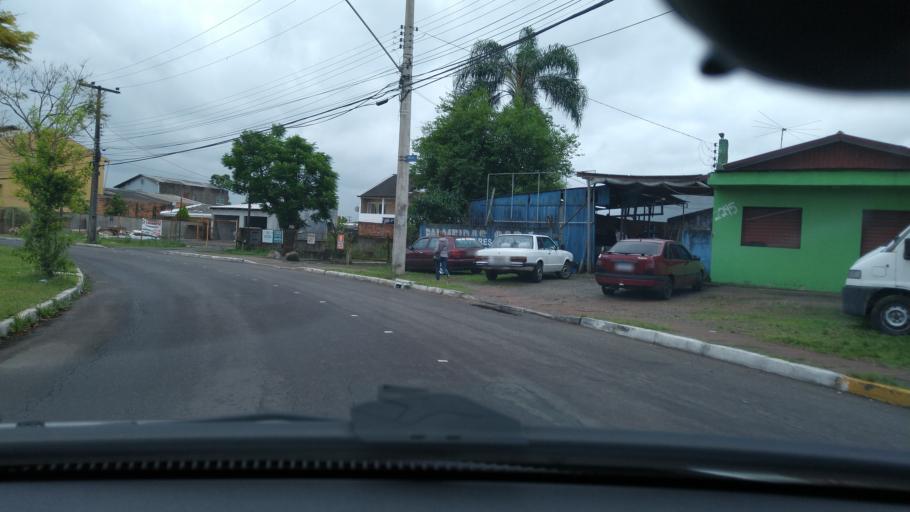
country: BR
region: Rio Grande do Sul
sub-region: Canoas
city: Canoas
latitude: -29.9016
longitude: -51.2033
